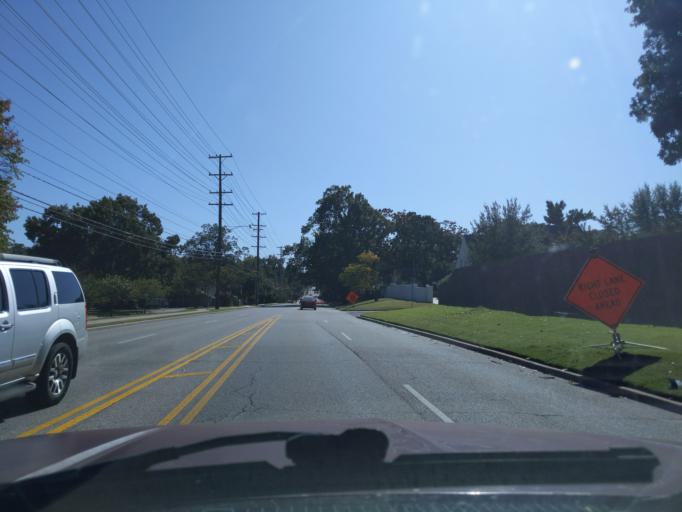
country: US
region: Oklahoma
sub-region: Tulsa County
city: Tulsa
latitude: 36.1178
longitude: -95.9580
